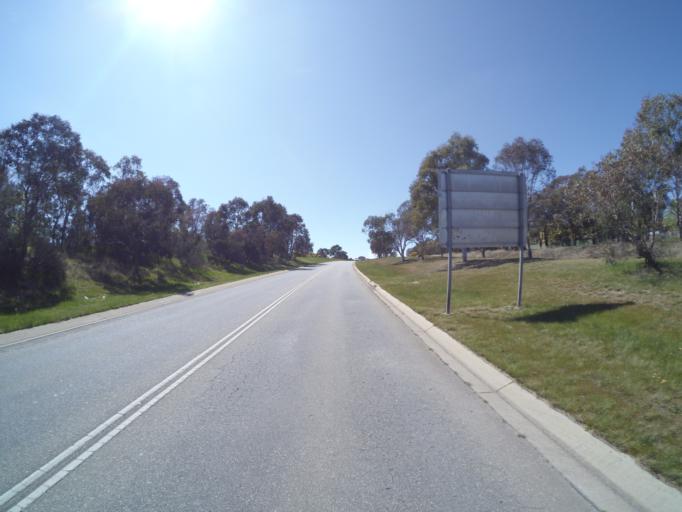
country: AU
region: Australian Capital Territory
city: Macarthur
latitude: -35.4331
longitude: 149.0987
